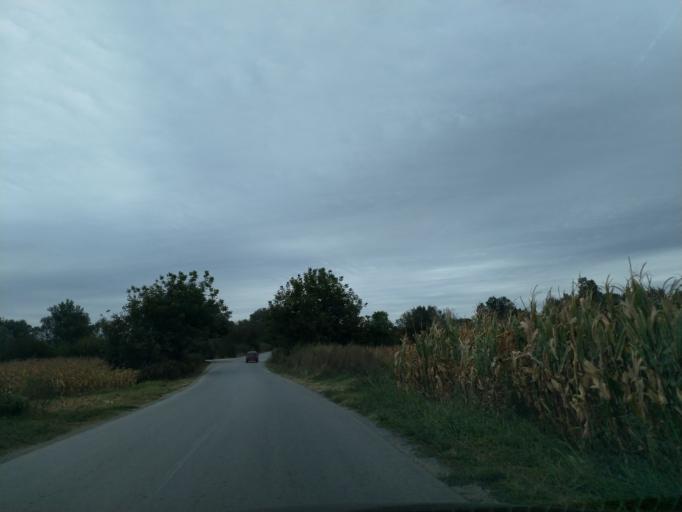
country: RS
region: Central Serbia
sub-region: Pomoravski Okrug
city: Paracin
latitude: 43.8295
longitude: 21.3402
